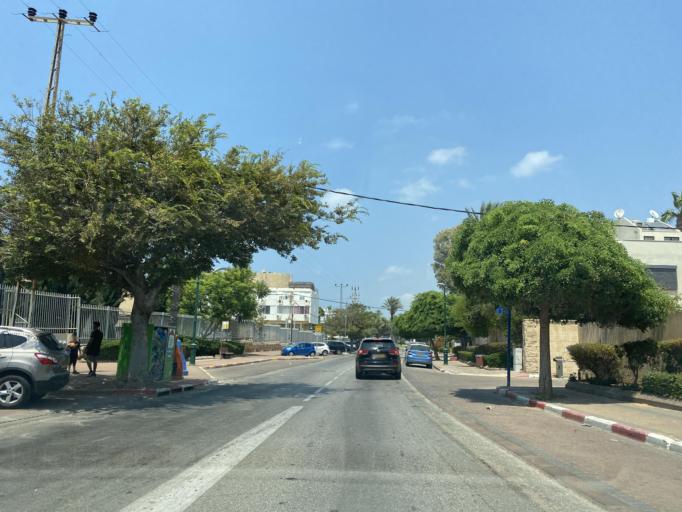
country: IL
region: Tel Aviv
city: Herzliya Pituah
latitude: 32.1688
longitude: 34.8034
